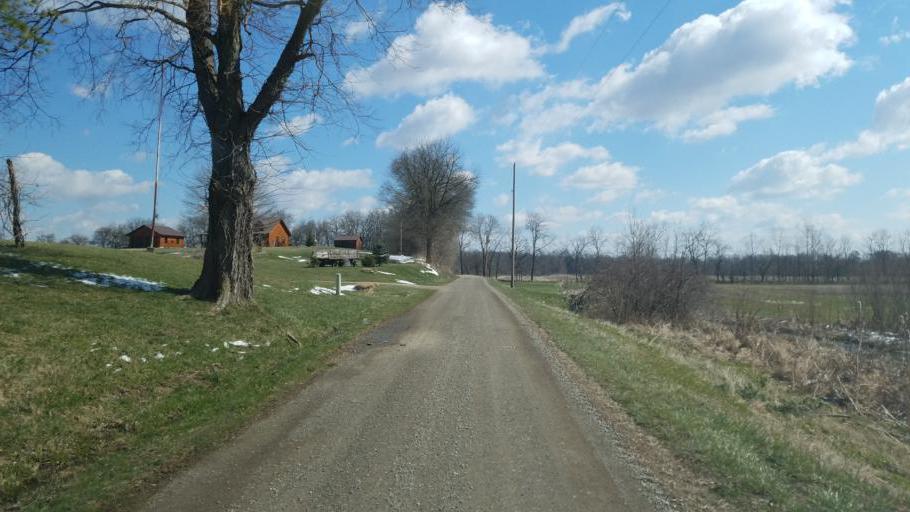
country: US
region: Ohio
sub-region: Licking County
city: Utica
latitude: 40.2593
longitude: -82.5025
